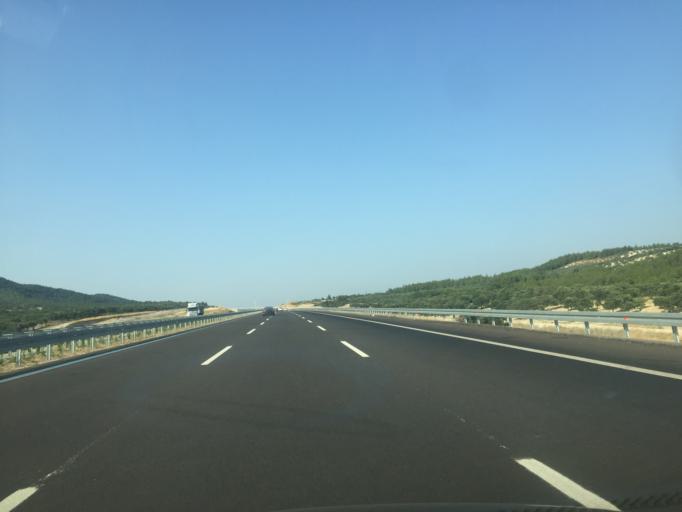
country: TR
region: Manisa
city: Zeytinliova
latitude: 38.9966
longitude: 27.7373
